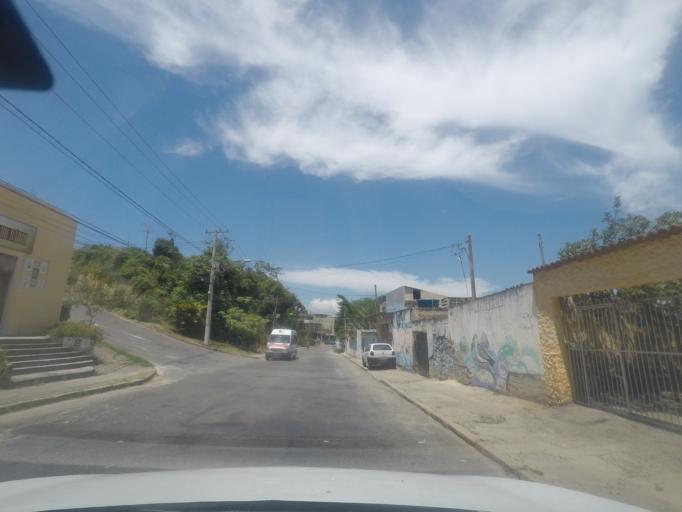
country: BR
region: Rio de Janeiro
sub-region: Itaguai
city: Itaguai
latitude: -22.9849
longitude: -43.6970
